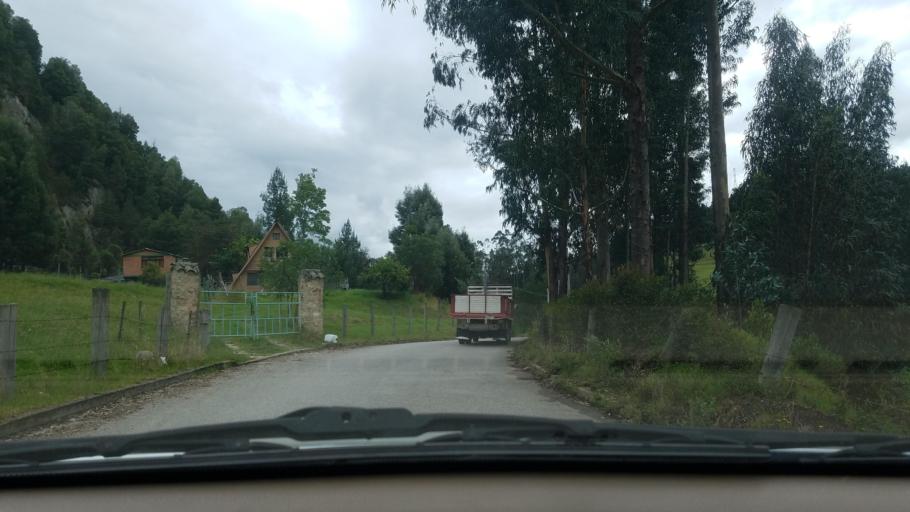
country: CO
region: Boyaca
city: Paipa
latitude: 5.7311
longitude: -73.1136
